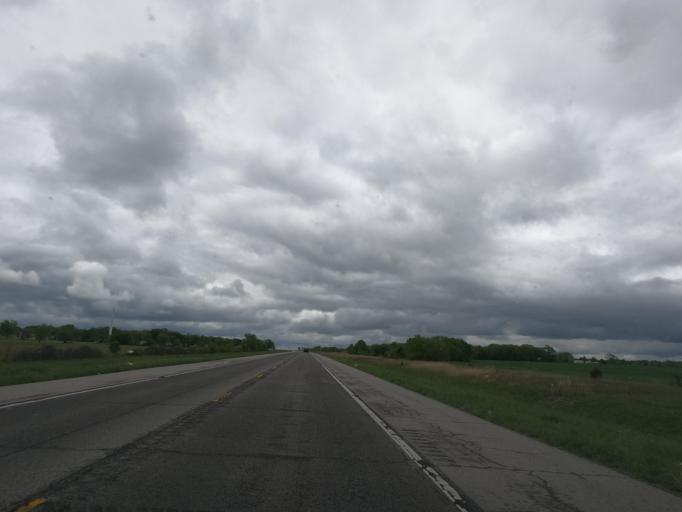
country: US
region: Kansas
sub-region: Montgomery County
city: Cherryvale
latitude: 37.3433
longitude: -95.4190
